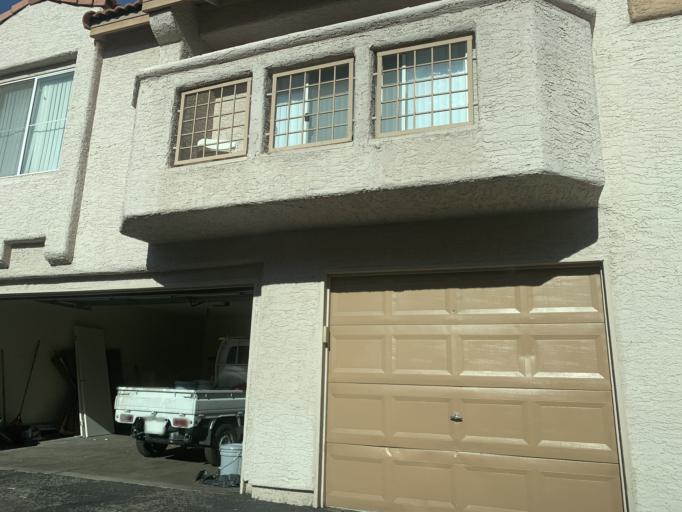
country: US
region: Nevada
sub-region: Clark County
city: Summerlin South
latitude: 36.1302
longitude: -115.2890
